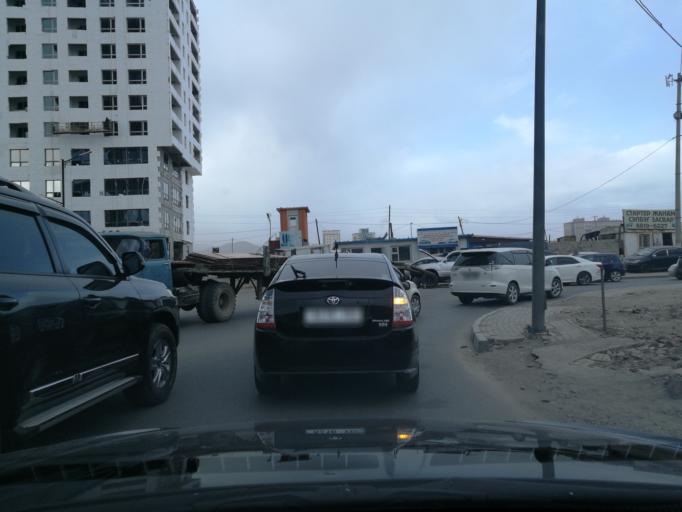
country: MN
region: Ulaanbaatar
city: Ulaanbaatar
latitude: 47.9322
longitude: 106.9137
